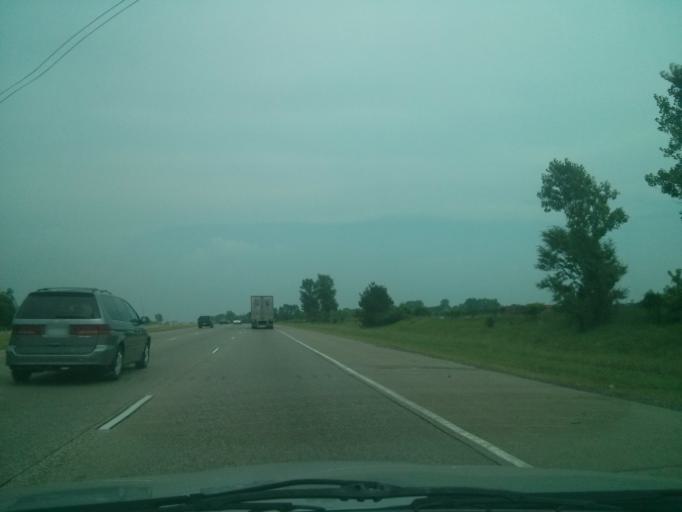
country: US
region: Minnesota
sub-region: Washington County
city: Lakeland
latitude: 44.9492
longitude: -92.8185
